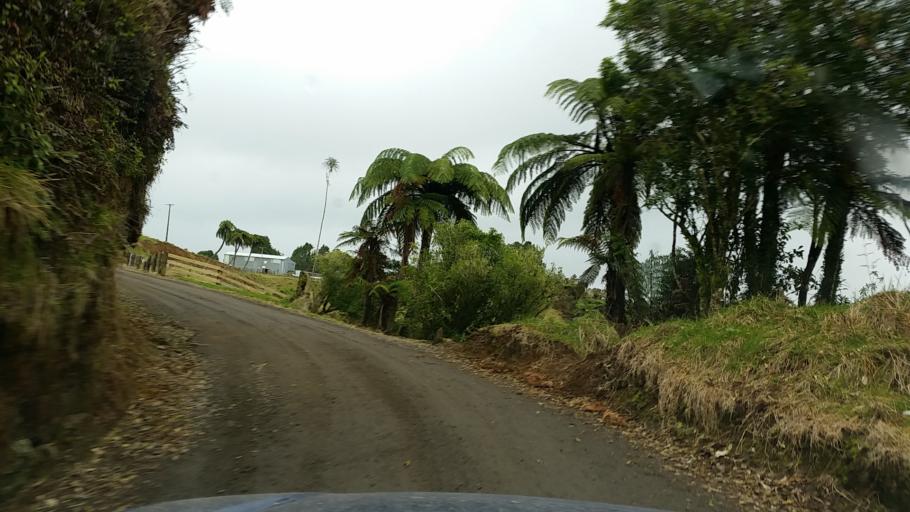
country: NZ
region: Taranaki
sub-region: South Taranaki District
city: Eltham
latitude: -39.1675
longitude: 174.6284
